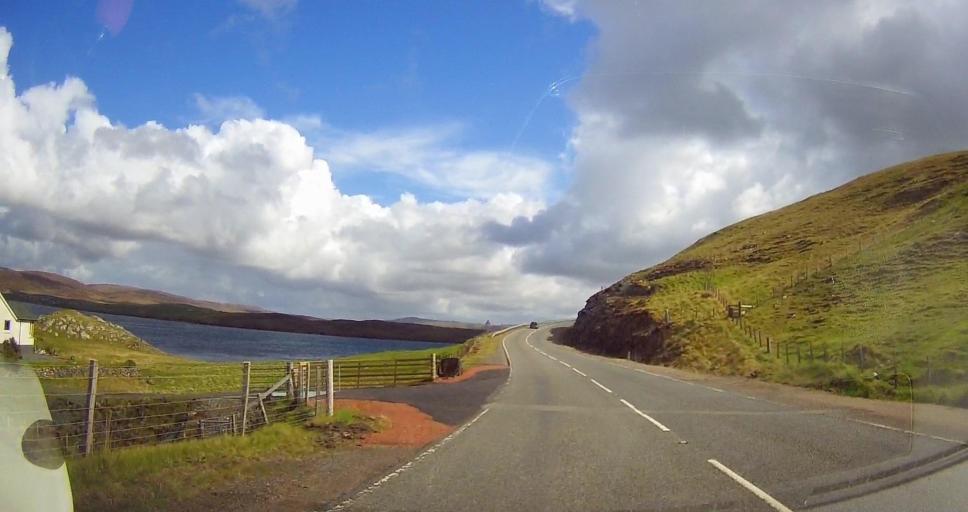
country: GB
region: Scotland
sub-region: Shetland Islands
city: Lerwick
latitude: 60.4039
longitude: -1.3855
